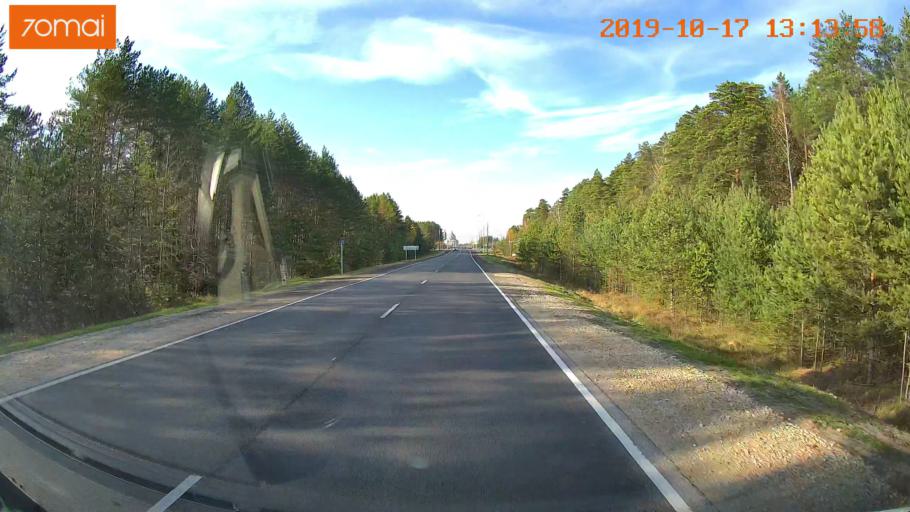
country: RU
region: Rjazan
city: Gus'-Zheleznyy
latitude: 55.0493
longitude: 41.1801
